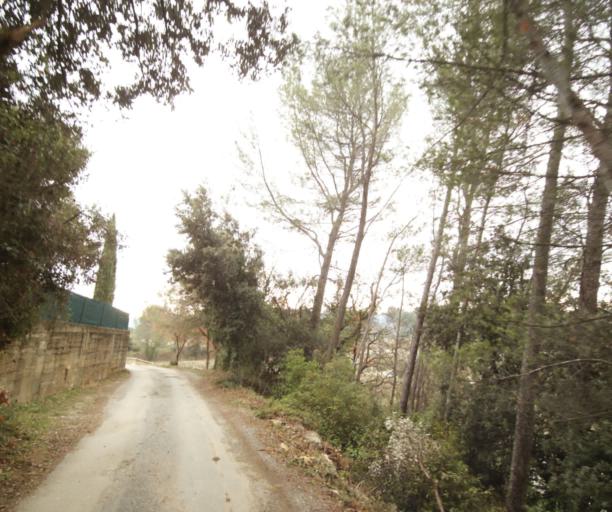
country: FR
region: Provence-Alpes-Cote d'Azur
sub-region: Departement du Var
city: Trans-en-Provence
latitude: 43.5125
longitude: 6.4823
